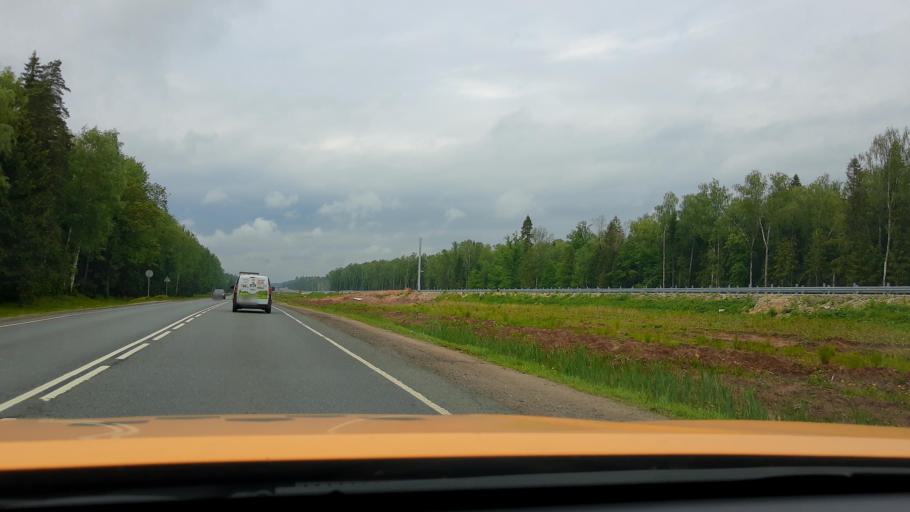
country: RU
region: Moskovskaya
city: Troitsk
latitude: 55.3906
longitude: 37.3454
